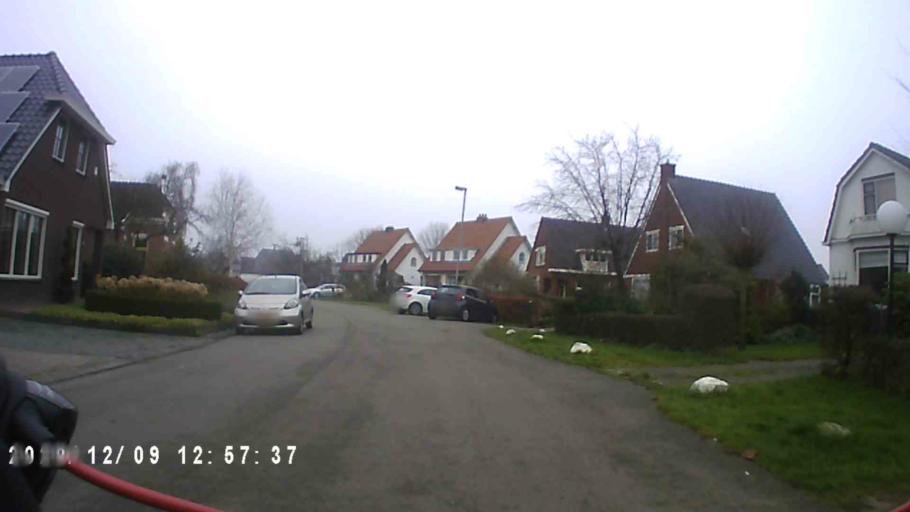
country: NL
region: Groningen
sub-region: Gemeente Groningen
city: Oosterpark
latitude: 53.2294
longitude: 6.6410
